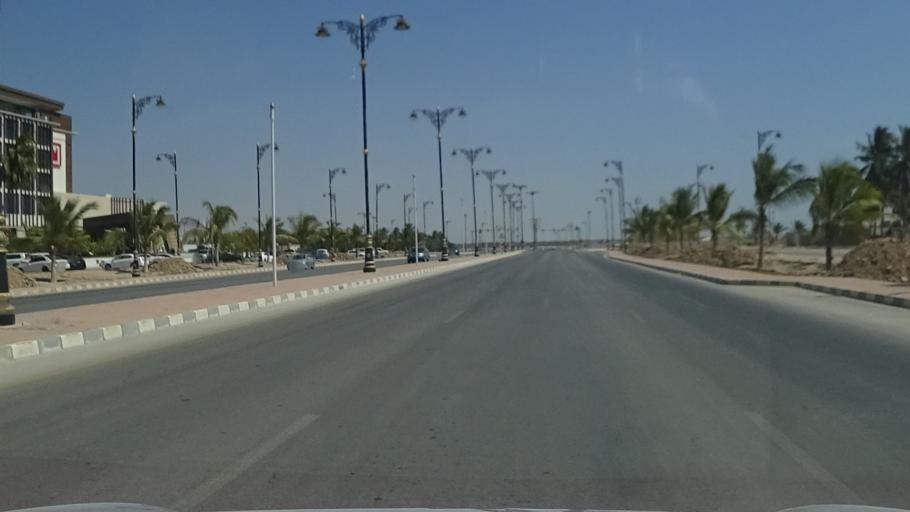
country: OM
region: Zufar
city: Salalah
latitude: 17.0359
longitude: 54.1691
